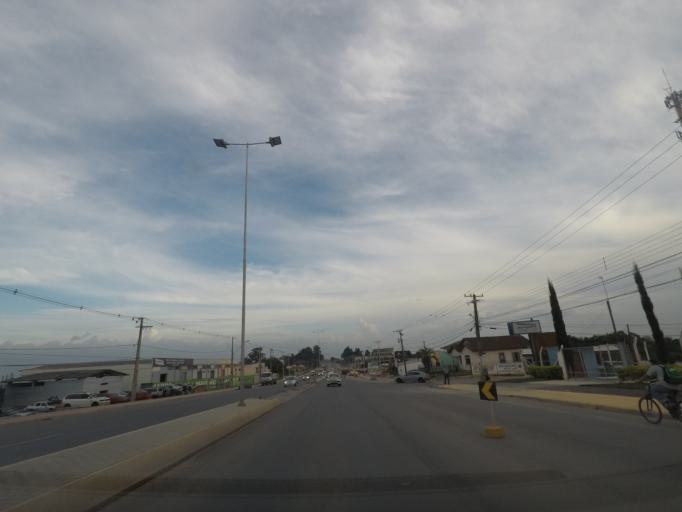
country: BR
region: Parana
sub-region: Colombo
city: Colombo
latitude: -25.3327
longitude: -49.2209
